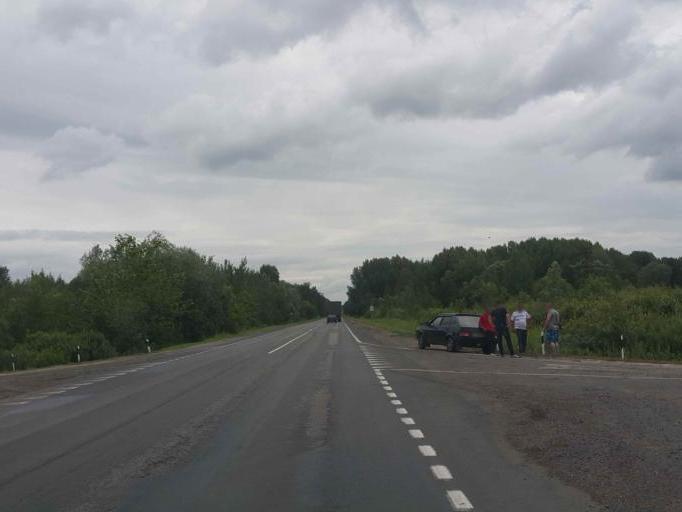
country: RU
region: Tambov
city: Zavoronezhskoye
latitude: 52.9421
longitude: 40.5962
